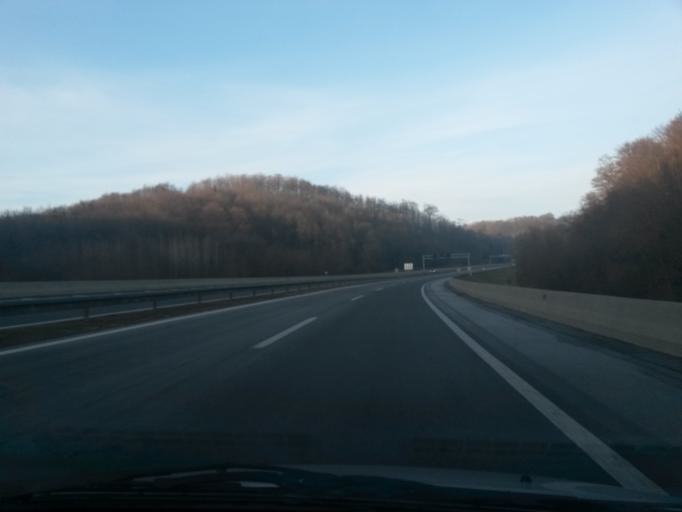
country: HR
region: Varazdinska
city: Ljubescica
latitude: 46.2145
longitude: 16.4043
